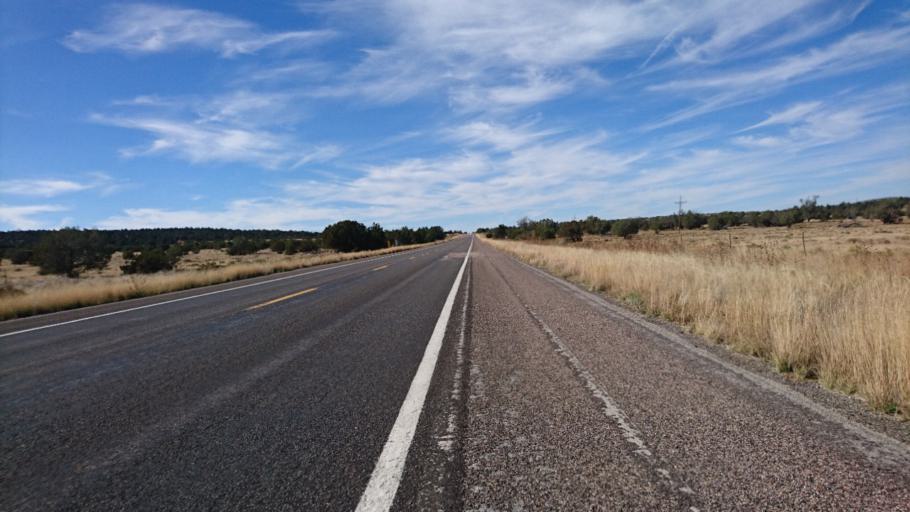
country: US
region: Arizona
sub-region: Mohave County
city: Peach Springs
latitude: 35.5056
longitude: -113.1805
